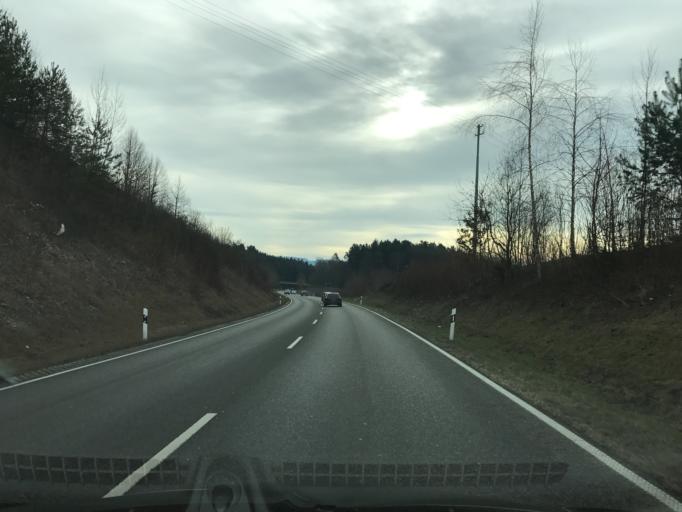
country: DE
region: Bavaria
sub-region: Swabia
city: Nonnenhorn
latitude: 47.5958
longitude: 9.6336
